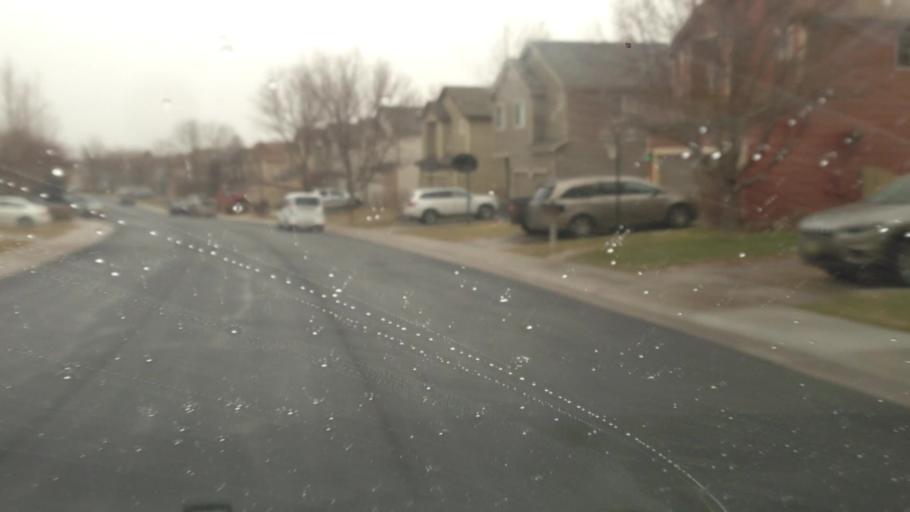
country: US
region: Colorado
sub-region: Douglas County
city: Stonegate
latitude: 39.5159
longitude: -104.7895
